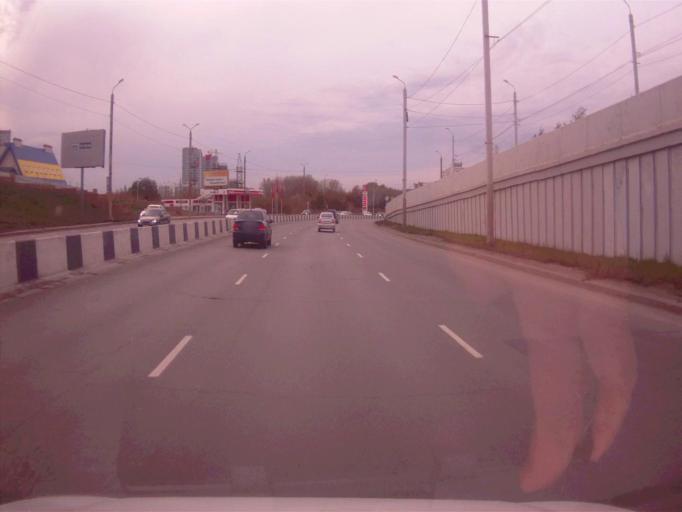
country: RU
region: Chelyabinsk
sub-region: Gorod Chelyabinsk
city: Chelyabinsk
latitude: 55.1741
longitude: 61.3853
